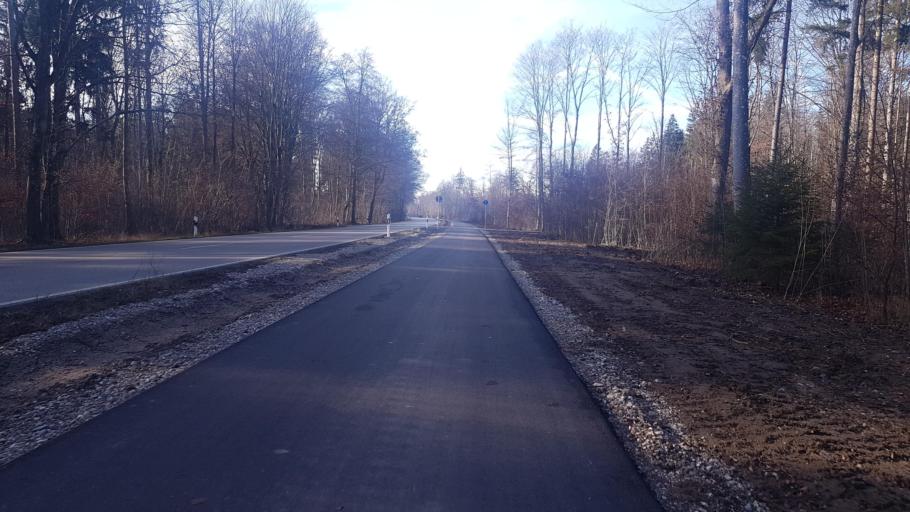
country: DE
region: Bavaria
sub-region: Upper Bavaria
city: Krailling
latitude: 48.0735
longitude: 11.4070
